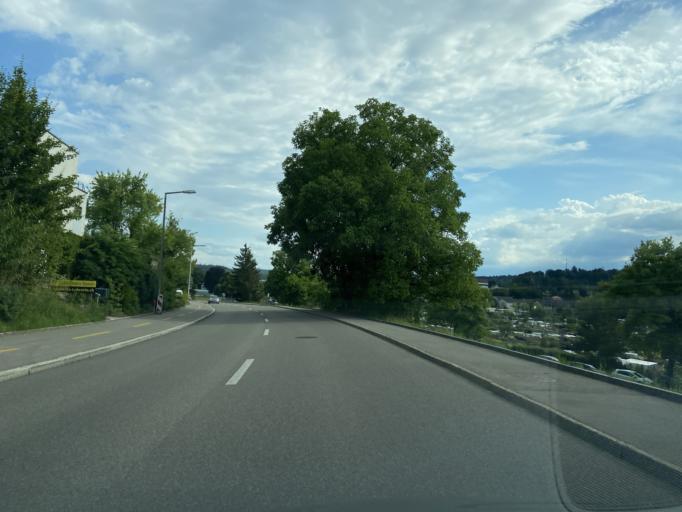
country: CH
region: Zurich
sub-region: Bezirk Winterthur
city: Veltheim
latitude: 47.5226
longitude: 8.7216
